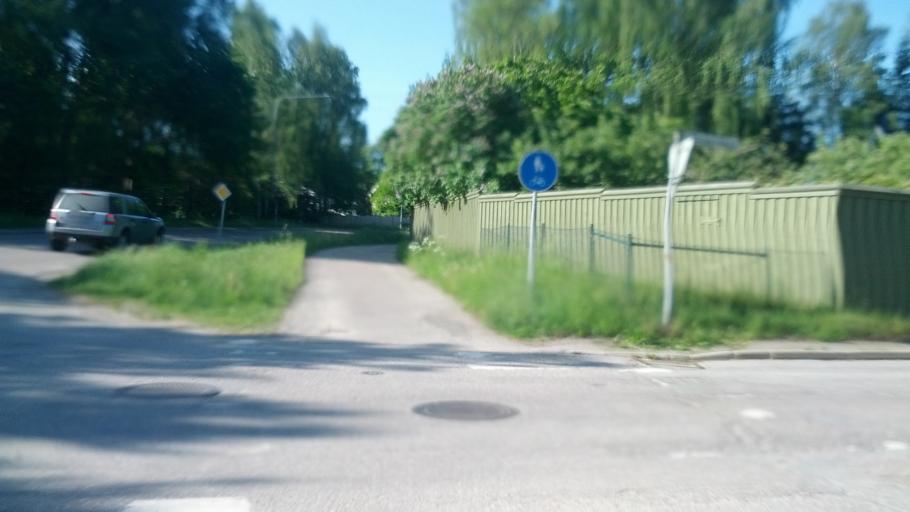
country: SE
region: Stockholm
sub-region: Taby Kommun
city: Taby
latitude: 59.4640
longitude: 18.0431
